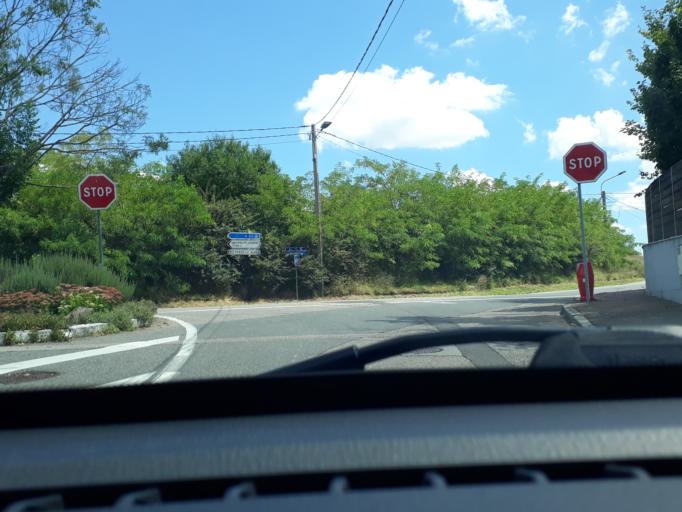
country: FR
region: Rhone-Alpes
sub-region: Departement du Rhone
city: Saint-Priest
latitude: 45.7071
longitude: 4.9298
